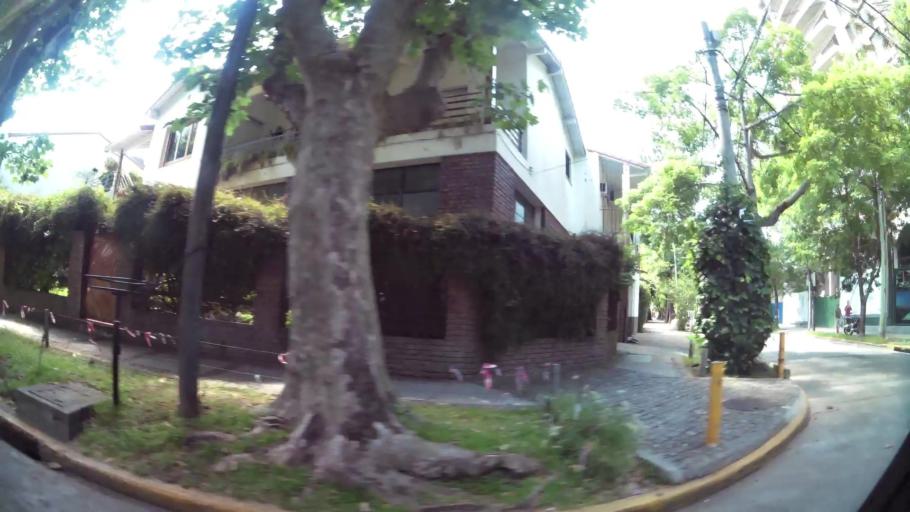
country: AR
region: Buenos Aires
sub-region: Partido de Tigre
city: Tigre
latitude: -34.4217
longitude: -58.5775
